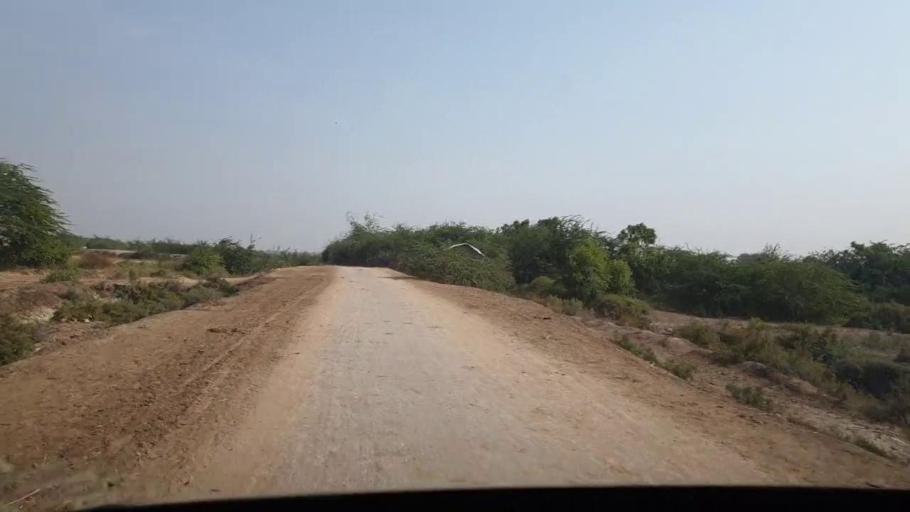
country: PK
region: Sindh
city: Chuhar Jamali
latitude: 24.2655
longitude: 67.9445
